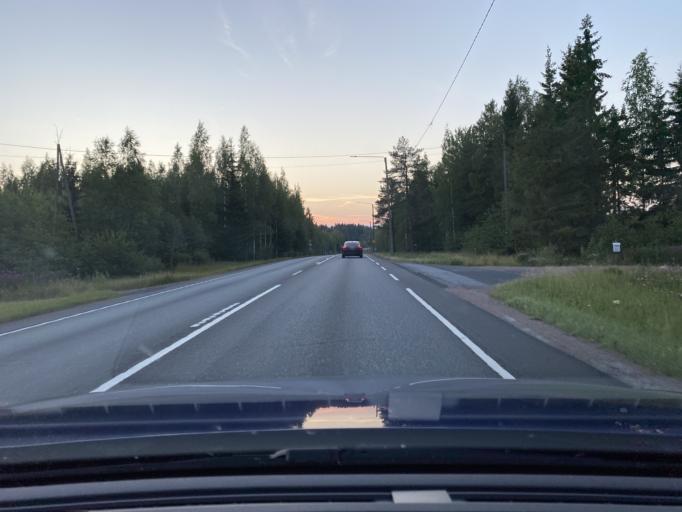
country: FI
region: Pirkanmaa
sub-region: Luoteis-Pirkanmaa
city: Ikaalinen
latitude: 61.8428
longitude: 22.9333
